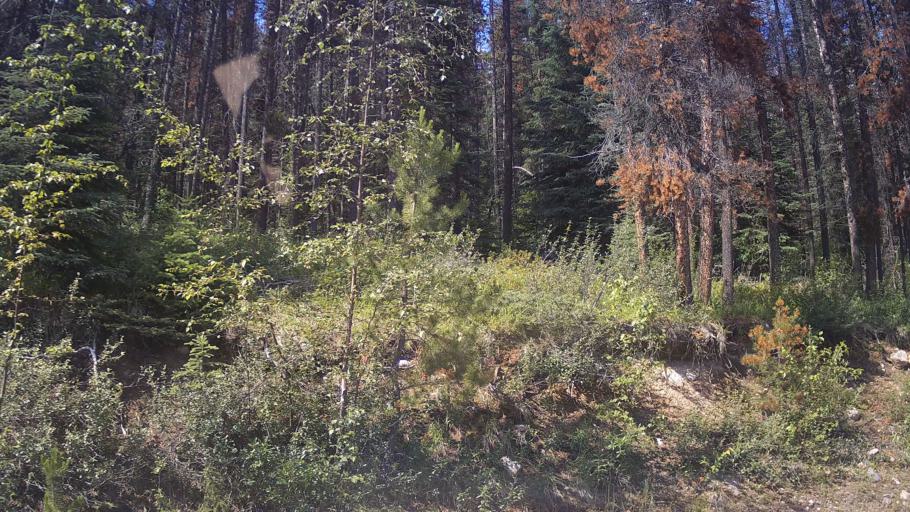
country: CA
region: Alberta
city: Jasper Park Lodge
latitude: 52.7693
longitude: -118.0316
